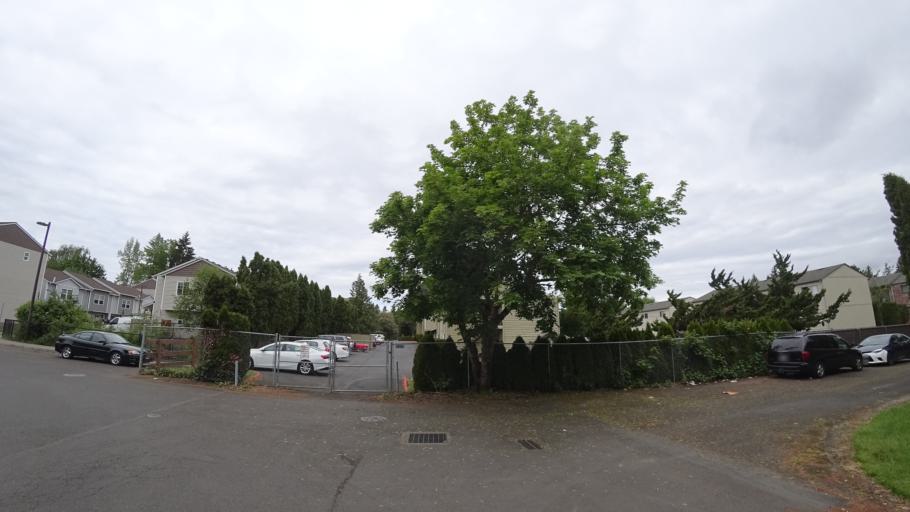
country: US
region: Oregon
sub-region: Washington County
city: Beaverton
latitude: 45.4734
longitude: -122.8028
